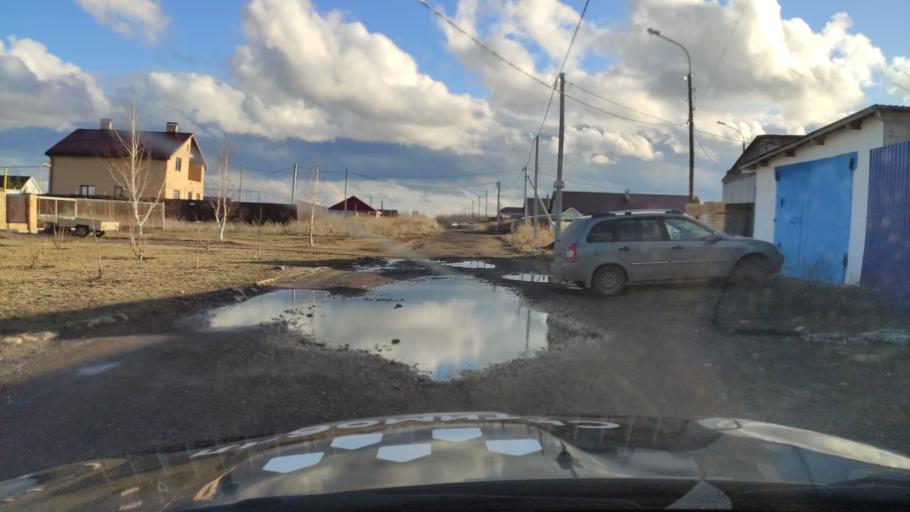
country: RU
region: Samara
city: Povolzhskiy
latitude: 53.5878
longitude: 49.7276
